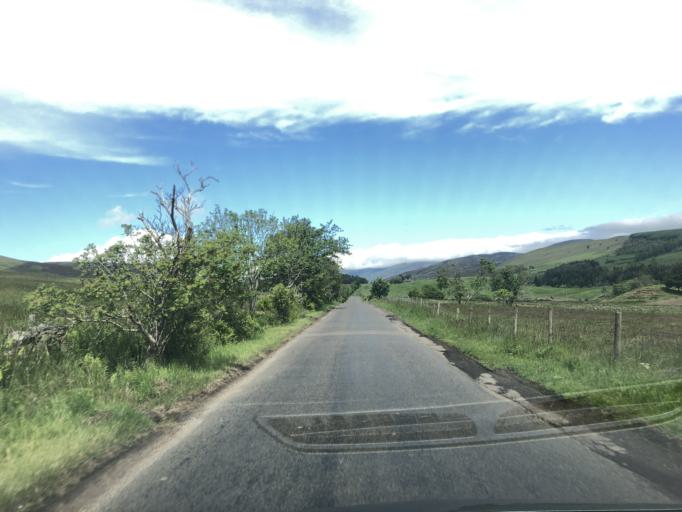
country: GB
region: Scotland
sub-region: Angus
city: Kirriemuir
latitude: 56.7497
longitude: -3.0143
